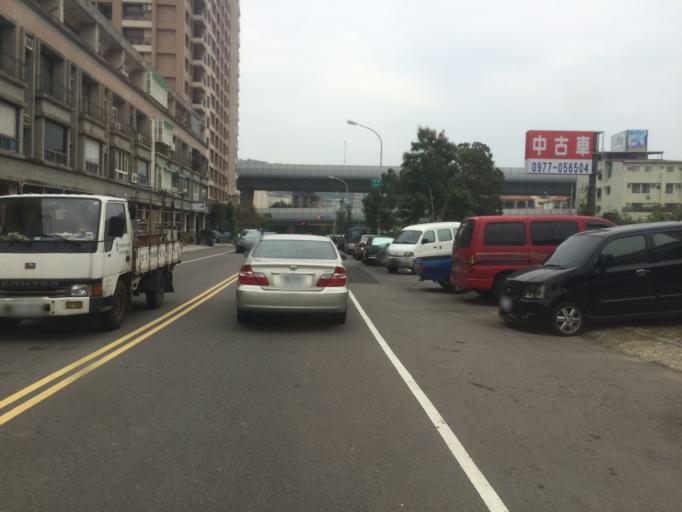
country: TW
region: Taiwan
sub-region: Taichung City
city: Taichung
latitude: 24.1801
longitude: 120.7199
